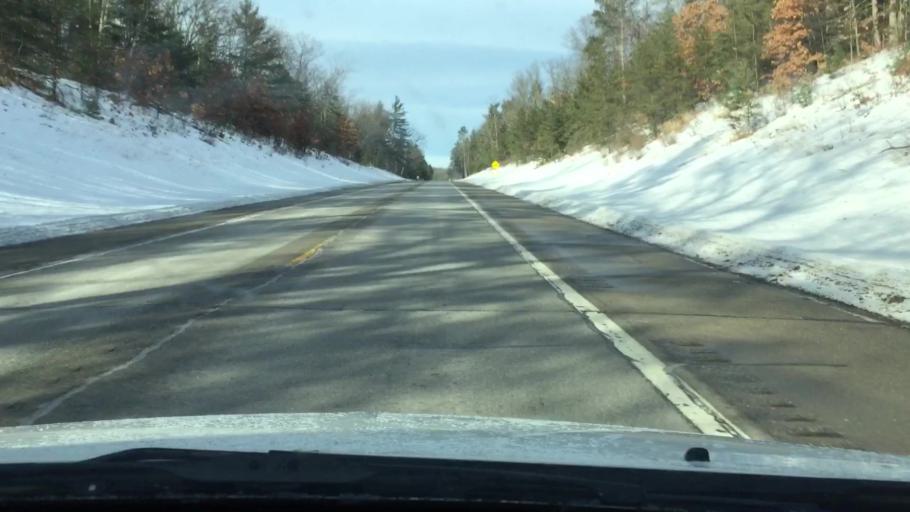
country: US
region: Michigan
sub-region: Wexford County
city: Manton
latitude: 44.5671
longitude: -85.3661
